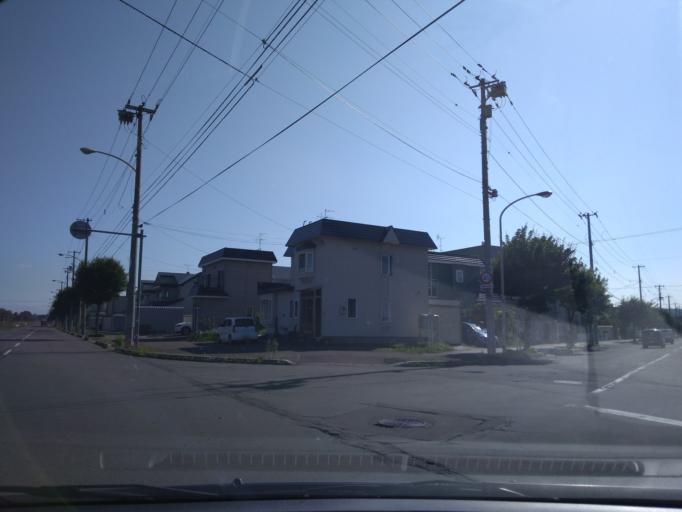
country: JP
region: Hokkaido
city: Kitahiroshima
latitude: 42.9883
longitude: 141.5762
